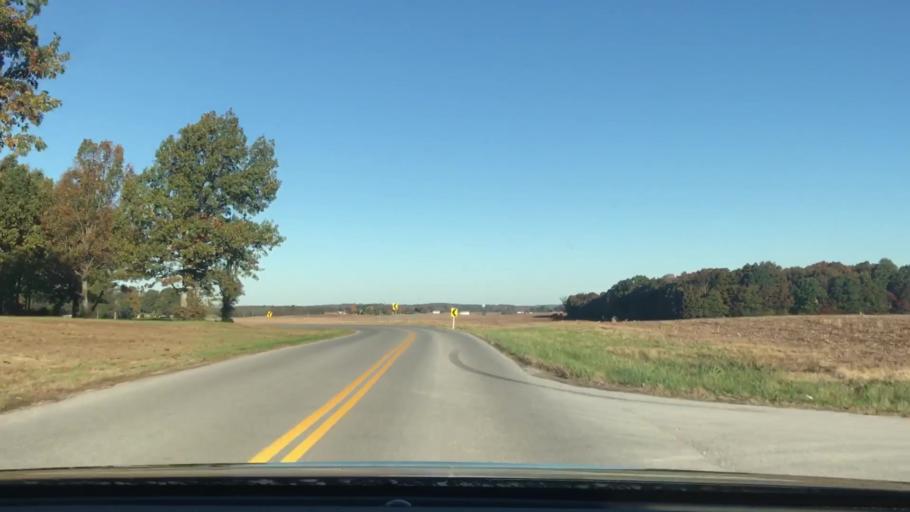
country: US
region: Kentucky
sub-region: Logan County
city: Auburn
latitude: 36.8279
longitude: -86.6771
